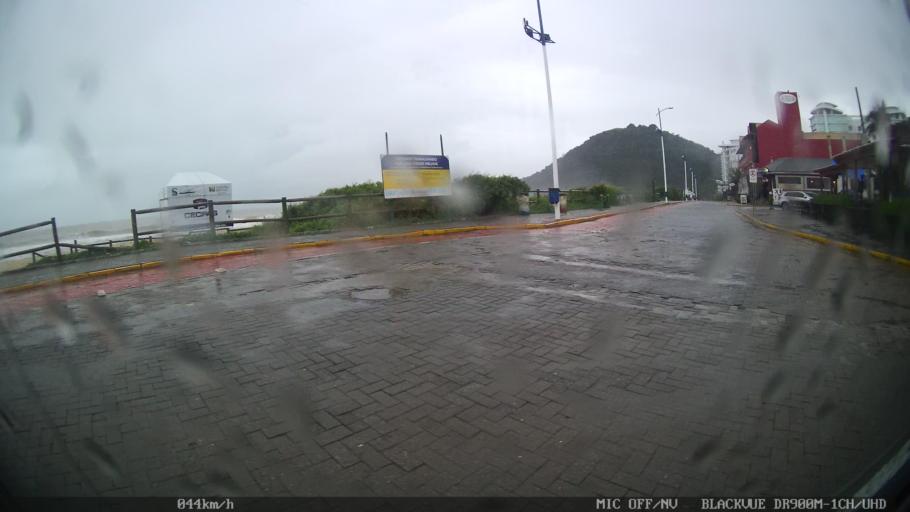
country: BR
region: Santa Catarina
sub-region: Balneario Camboriu
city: Balneario Camboriu
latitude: -26.9565
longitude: -48.6296
